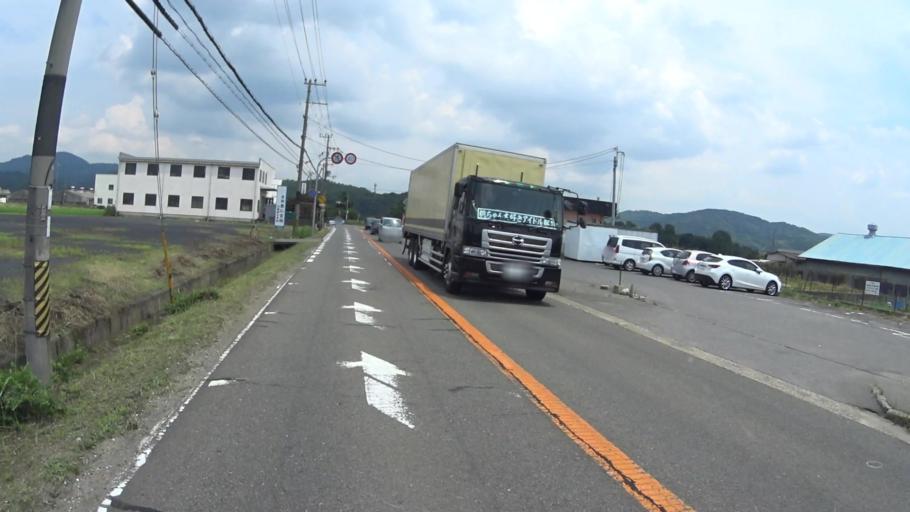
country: JP
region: Nara
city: Nara-shi
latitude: 34.7638
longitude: 135.8620
